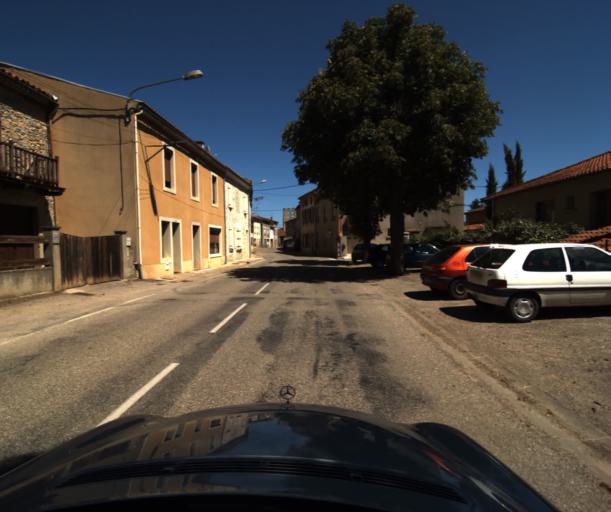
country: FR
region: Midi-Pyrenees
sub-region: Departement de l'Ariege
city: Belesta
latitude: 42.9564
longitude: 1.9189
